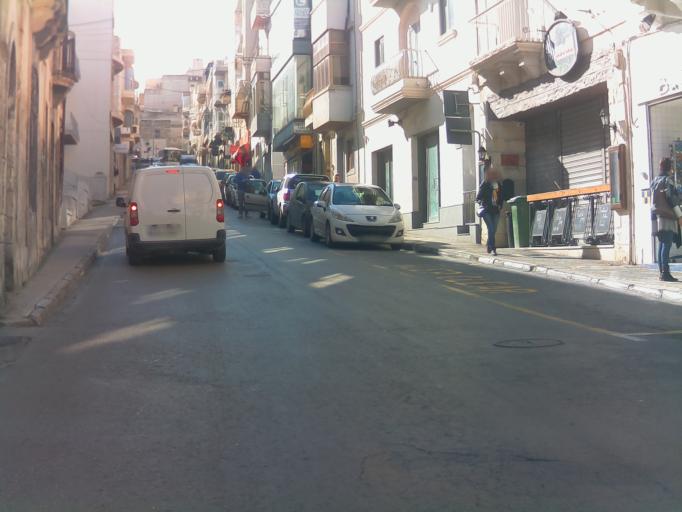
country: MT
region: Il-Mellieha
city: Mellieha
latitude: 35.9585
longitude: 14.3619
